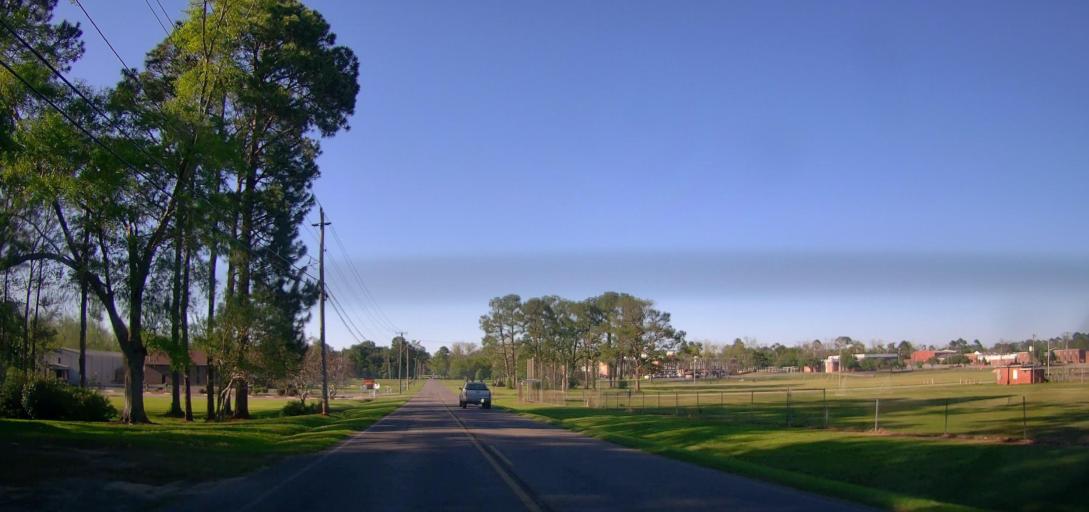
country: US
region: Georgia
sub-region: Ben Hill County
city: Fitzgerald
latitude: 31.7071
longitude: -83.2648
